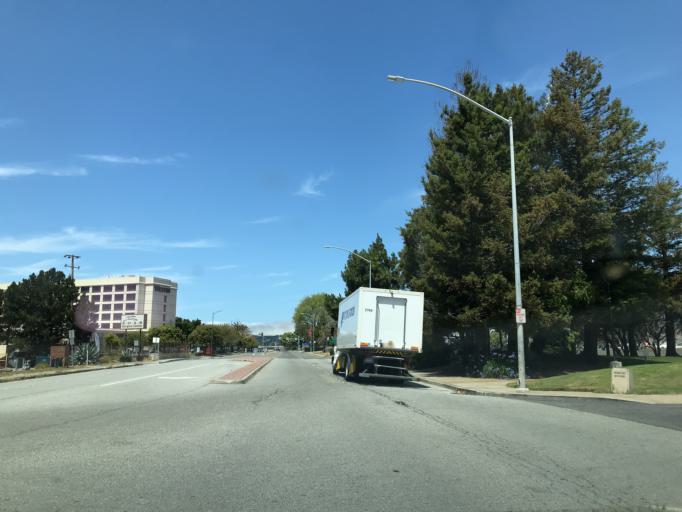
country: US
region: California
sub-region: San Mateo County
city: Millbrae
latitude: 37.6032
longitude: -122.3734
